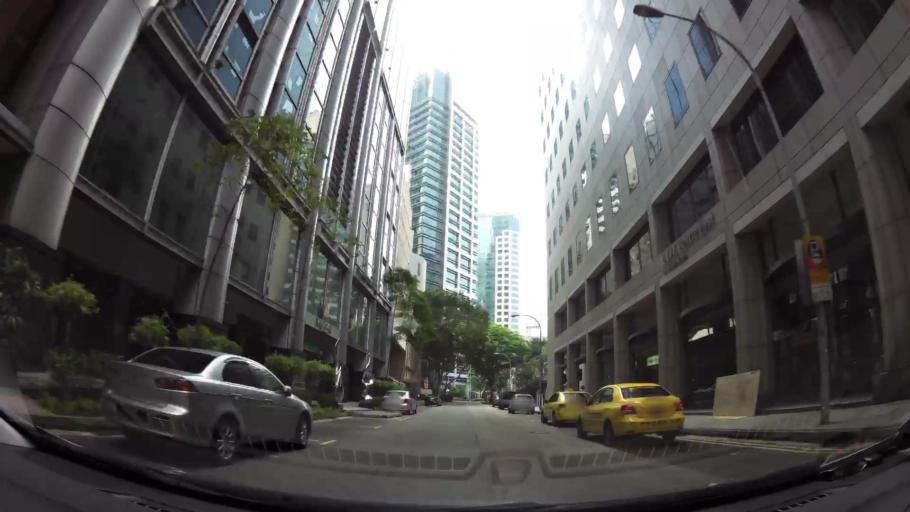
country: SG
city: Singapore
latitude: 1.2850
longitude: 103.8501
